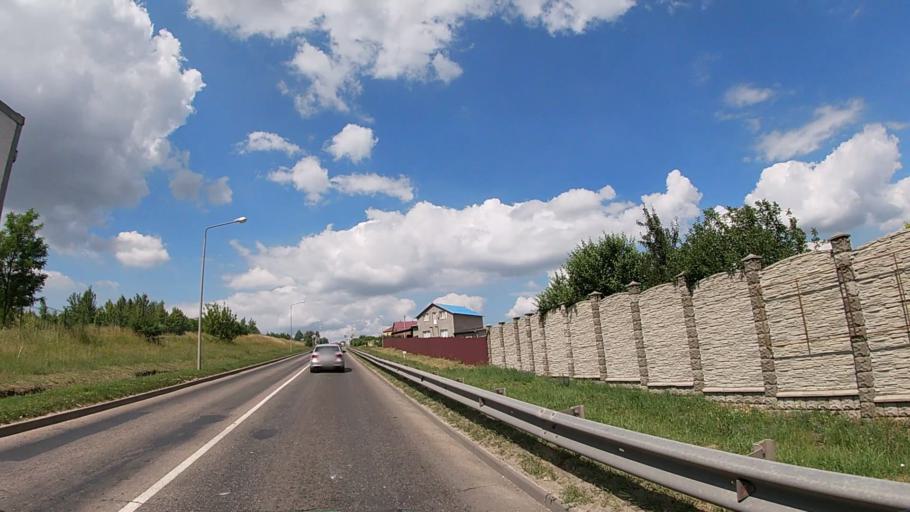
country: RU
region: Belgorod
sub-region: Belgorodskiy Rayon
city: Belgorod
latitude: 50.5950
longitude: 36.5451
